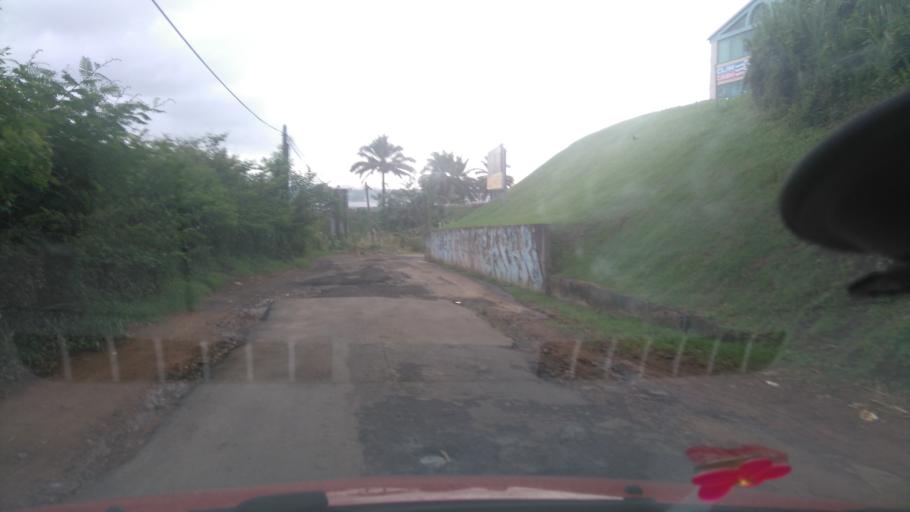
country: MQ
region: Martinique
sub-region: Martinique
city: Ducos
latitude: 14.5538
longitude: -60.9701
